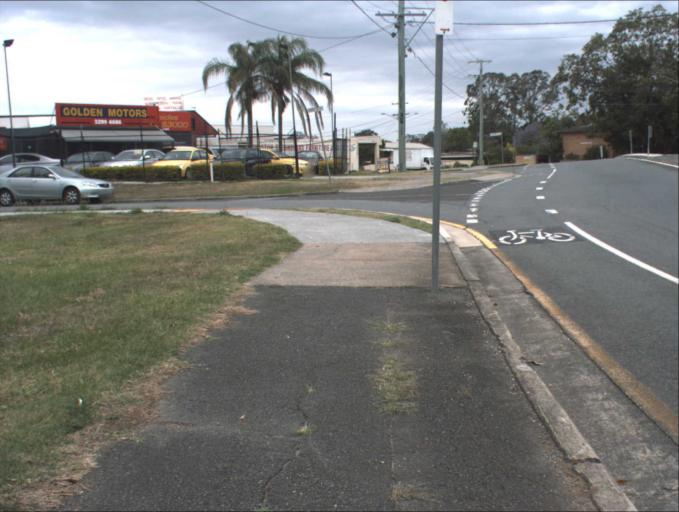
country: AU
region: Queensland
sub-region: Logan
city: Logan City
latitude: -27.6574
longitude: 153.1149
